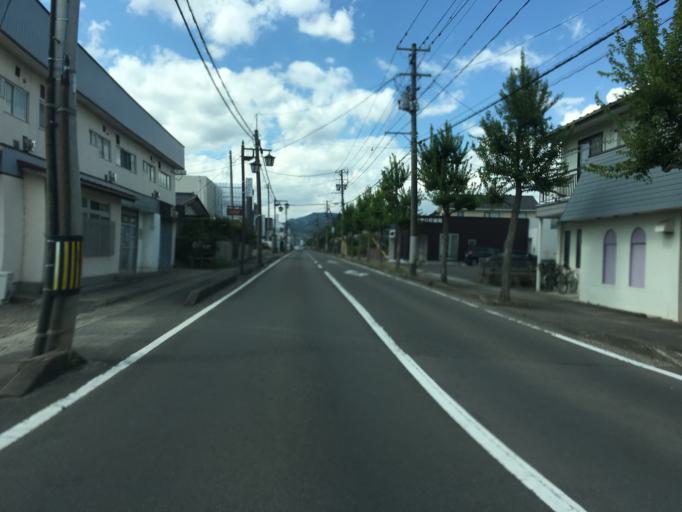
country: JP
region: Fukushima
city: Fukushima-shi
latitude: 37.7946
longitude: 140.4381
